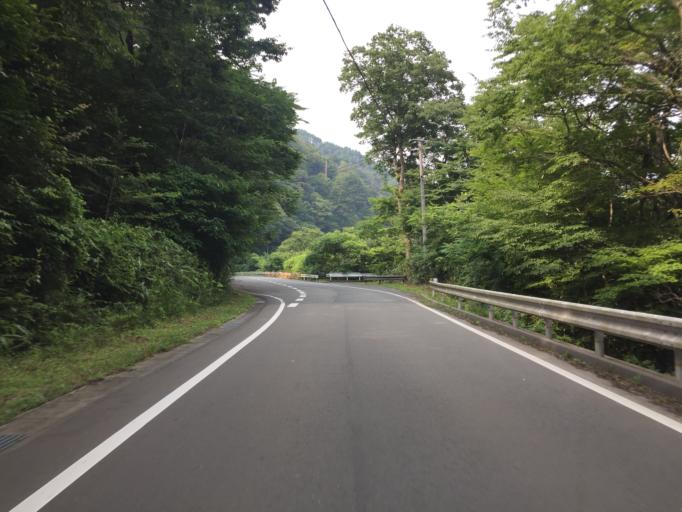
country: JP
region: Fukushima
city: Namie
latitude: 37.5757
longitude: 140.8825
